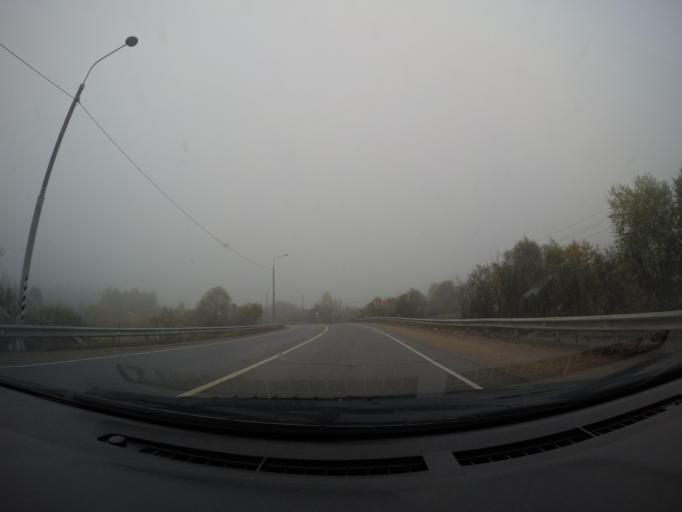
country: RU
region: Moskovskaya
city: Ruza
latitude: 55.7292
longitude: 36.3076
